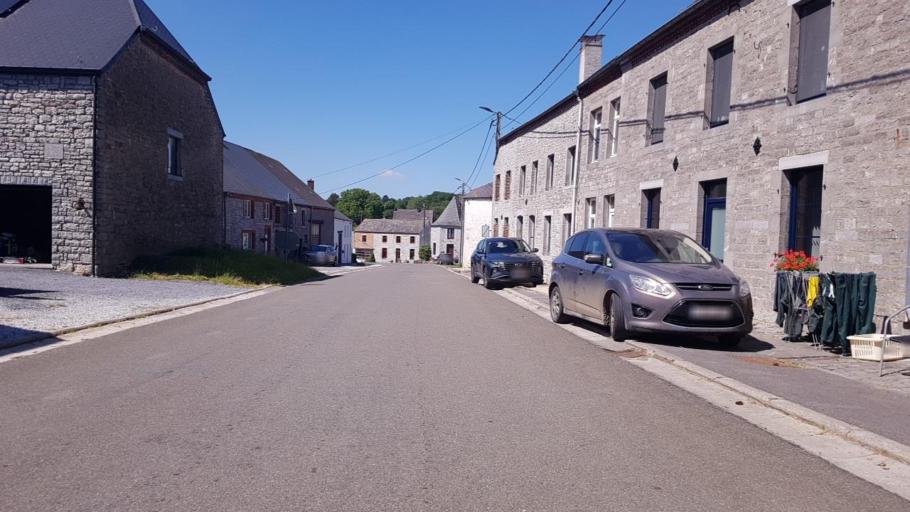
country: BE
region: Wallonia
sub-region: Province du Hainaut
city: Chimay
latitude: 50.0691
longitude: 4.2378
